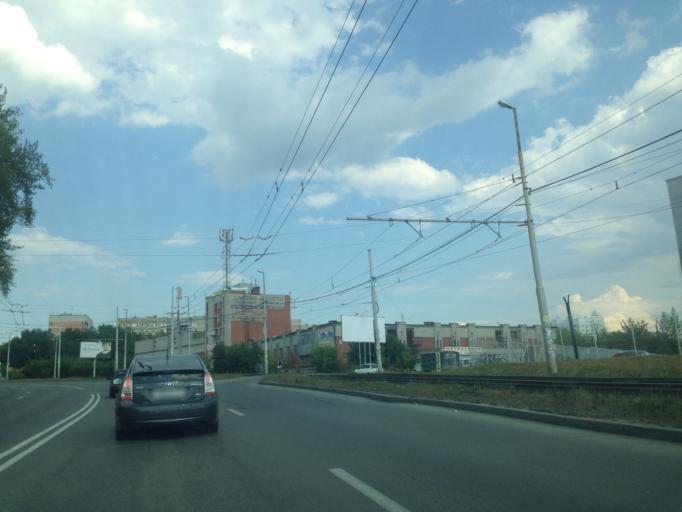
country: RU
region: Sverdlovsk
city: Yekaterinburg
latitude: 56.8576
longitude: 60.6163
